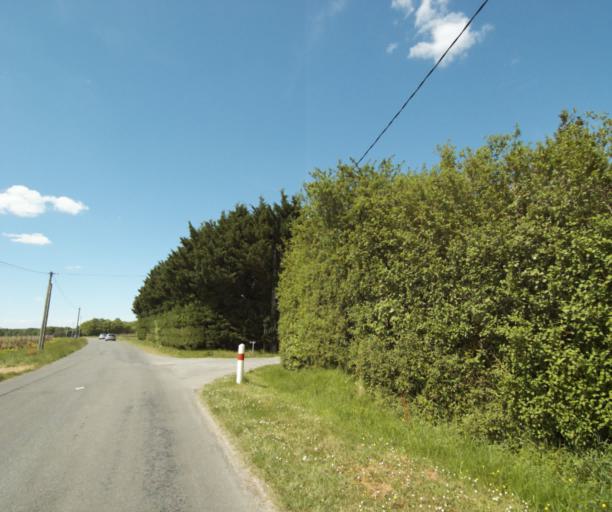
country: FR
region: Poitou-Charentes
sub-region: Departement de la Charente-Maritime
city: Burie
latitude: 45.7623
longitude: -0.4754
